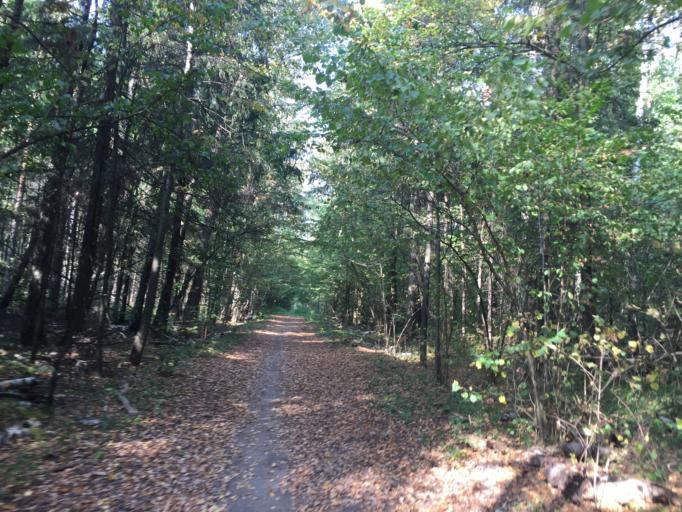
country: RU
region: Moscow
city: Babushkin
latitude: 55.8670
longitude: 37.7424
